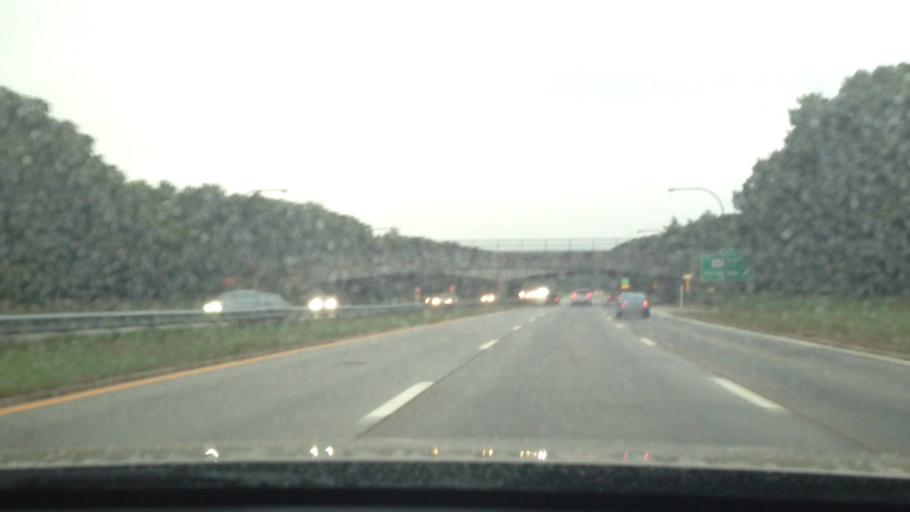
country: US
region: New York
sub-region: Suffolk County
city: Islip Terrace
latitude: 40.7556
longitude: -73.2108
